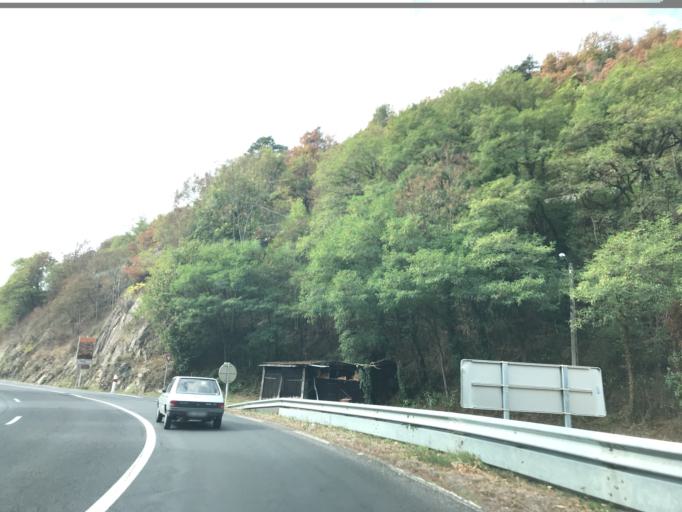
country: FR
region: Auvergne
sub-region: Departement du Puy-de-Dome
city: Thiers
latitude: 45.8654
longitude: 3.5620
